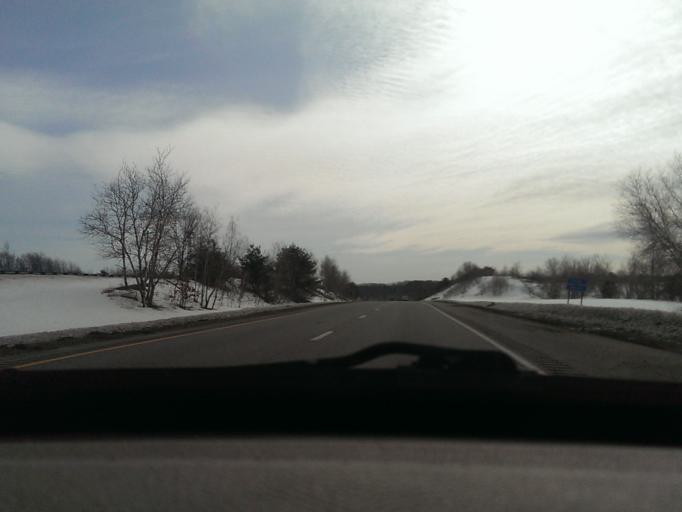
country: US
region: Massachusetts
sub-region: Worcester County
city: East Douglas
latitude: 42.1081
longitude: -71.7055
